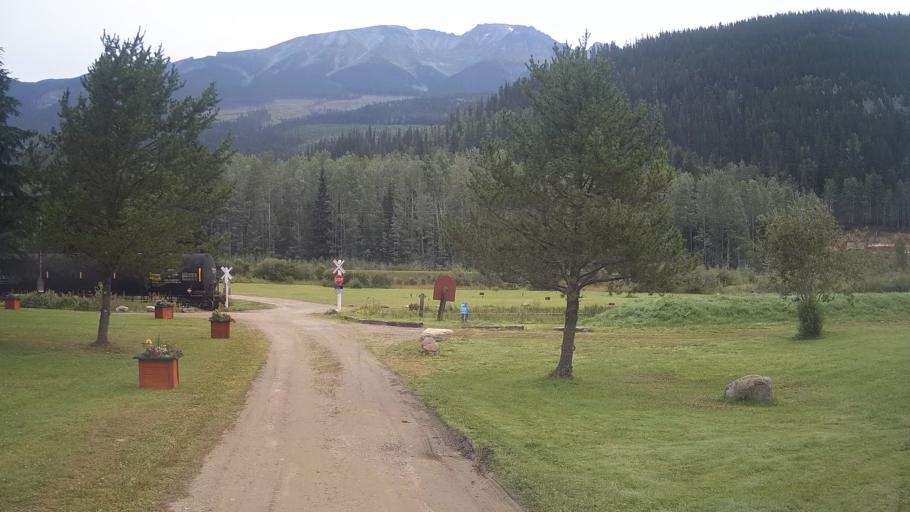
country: CA
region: Alberta
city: Jasper Park Lodge
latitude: 52.6563
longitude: -119.1938
